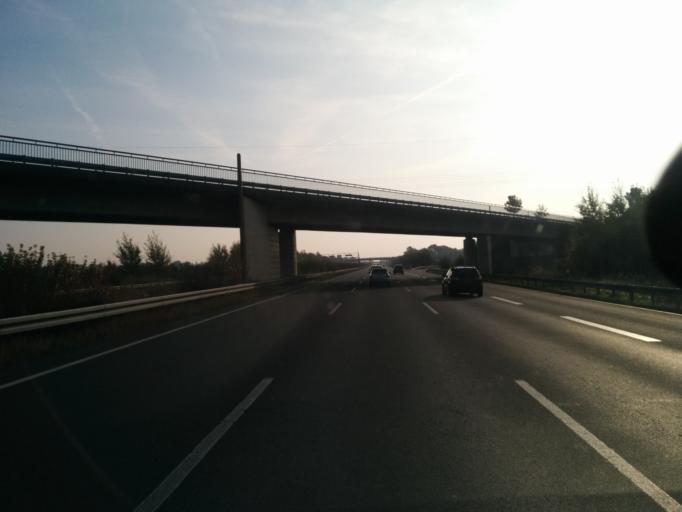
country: DE
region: Lower Saxony
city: Dollbergen
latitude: 52.3612
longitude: 10.1500
